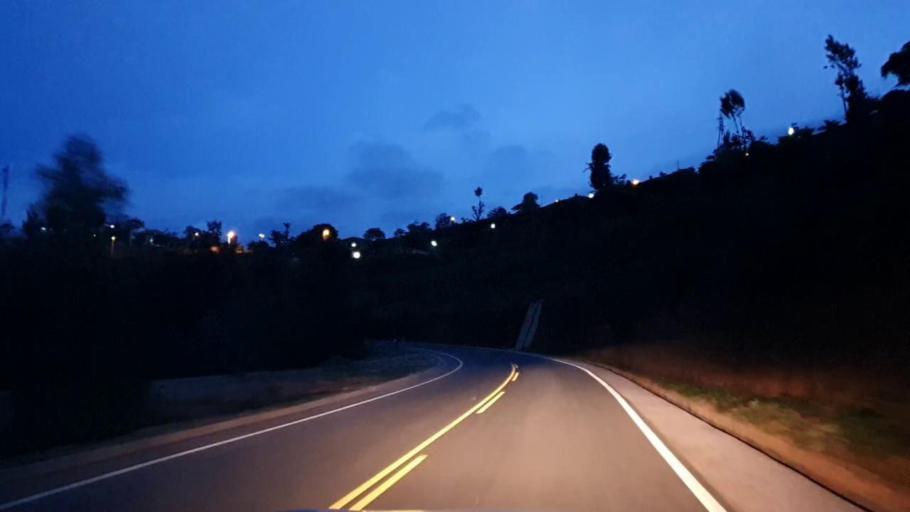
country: RW
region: Southern Province
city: Gikongoro
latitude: -2.4661
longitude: 29.5700
